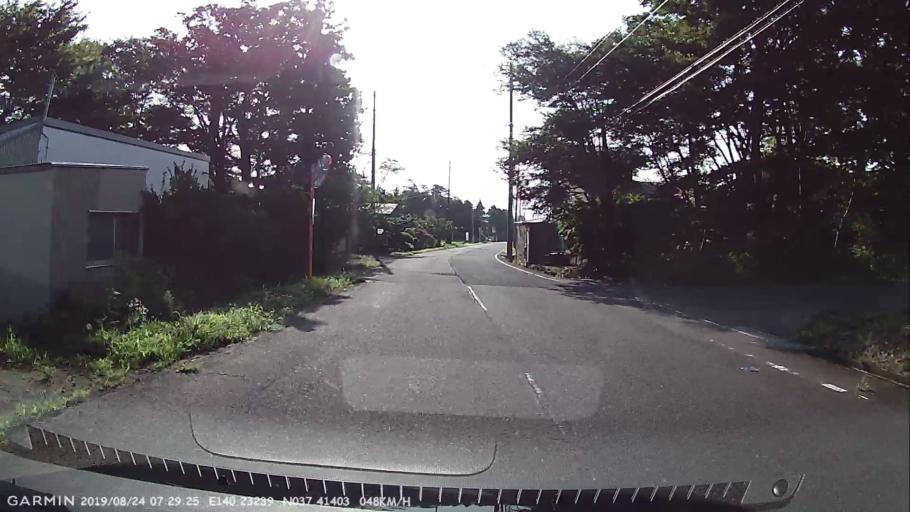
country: JP
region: Fukushima
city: Koriyama
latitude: 37.4140
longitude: 140.2325
